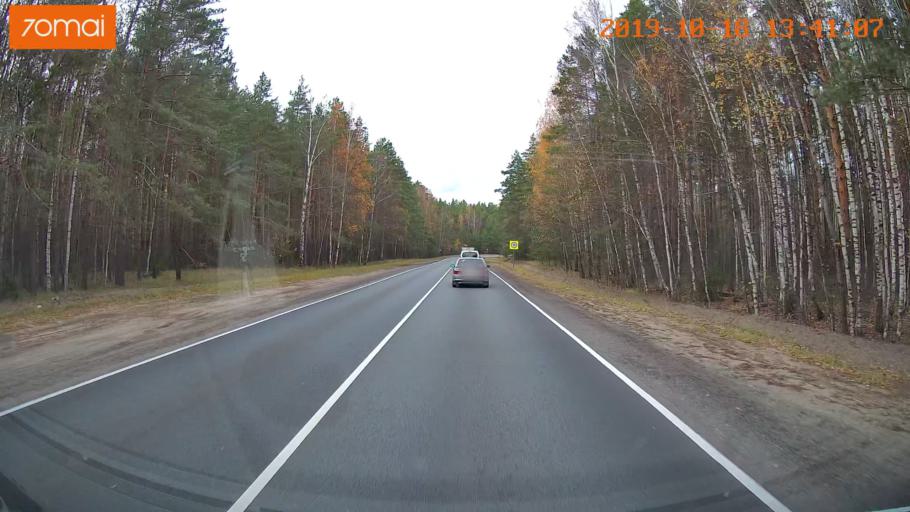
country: RU
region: Rjazan
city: Solotcha
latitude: 54.9174
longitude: 39.9972
